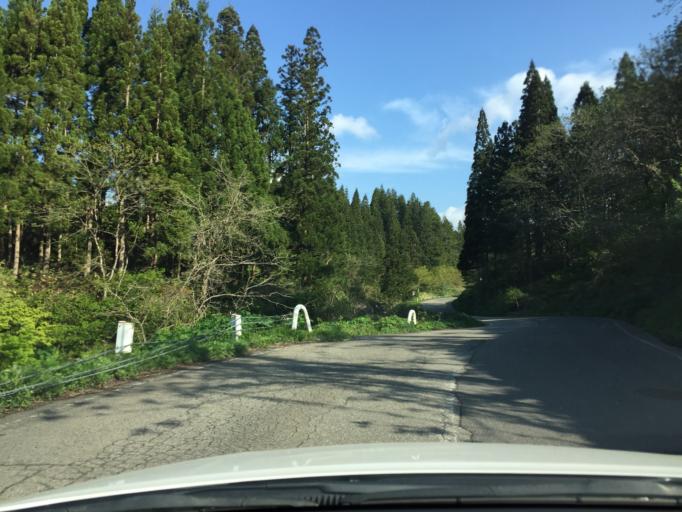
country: JP
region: Fukushima
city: Kitakata
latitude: 37.6878
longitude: 139.7173
